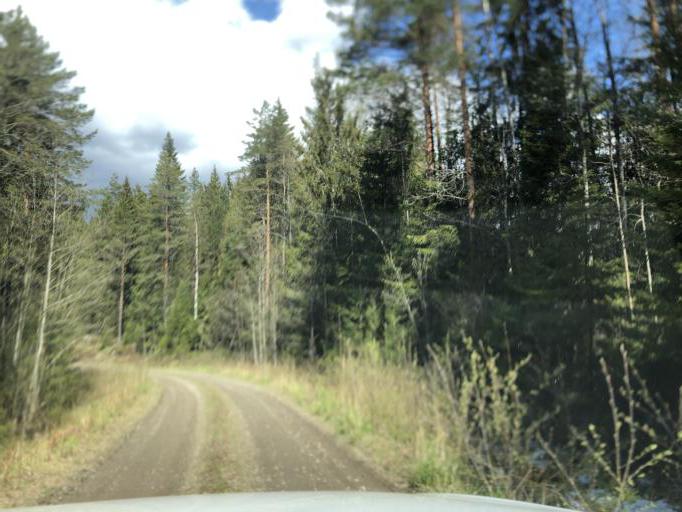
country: SE
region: Dalarna
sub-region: Avesta Kommun
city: Horndal
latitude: 60.2319
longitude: 16.6018
